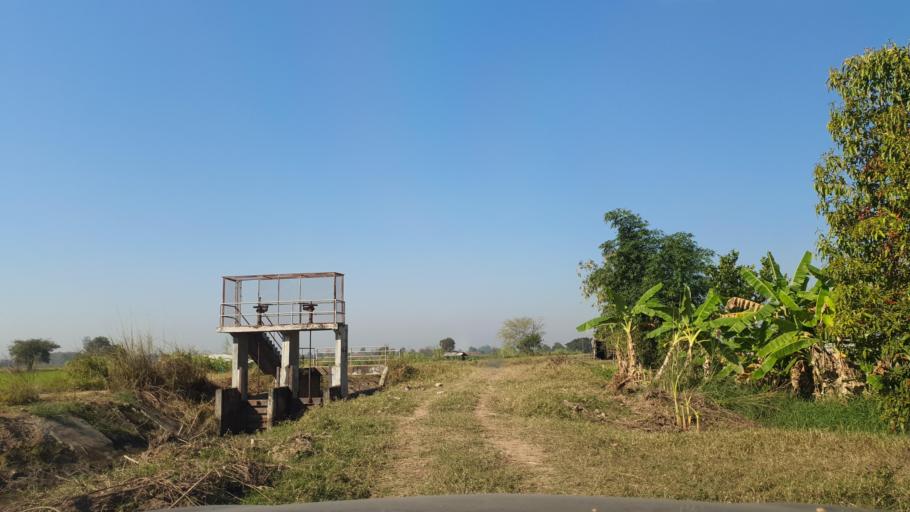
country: TH
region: Chiang Mai
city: San Kamphaeng
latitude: 18.7171
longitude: 99.1691
